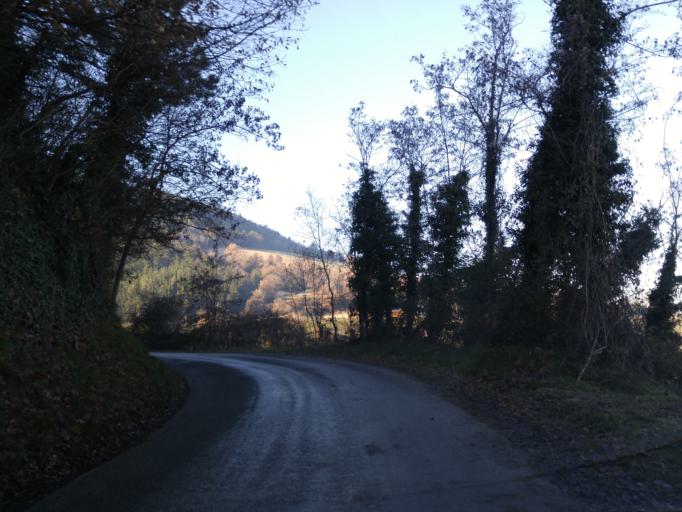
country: IT
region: The Marches
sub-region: Provincia di Pesaro e Urbino
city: Fossombrone
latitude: 43.6989
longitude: 12.7943
